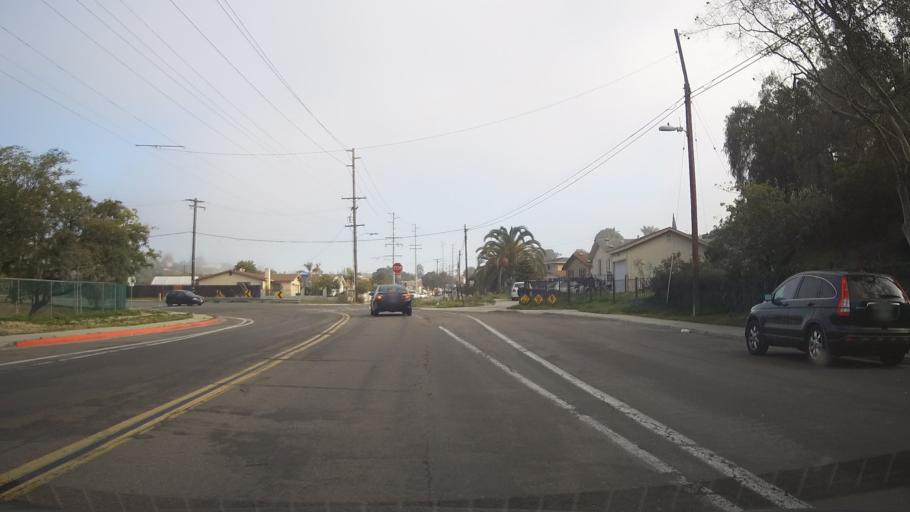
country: US
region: California
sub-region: San Diego County
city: Lemon Grove
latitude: 32.7350
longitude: -117.0873
